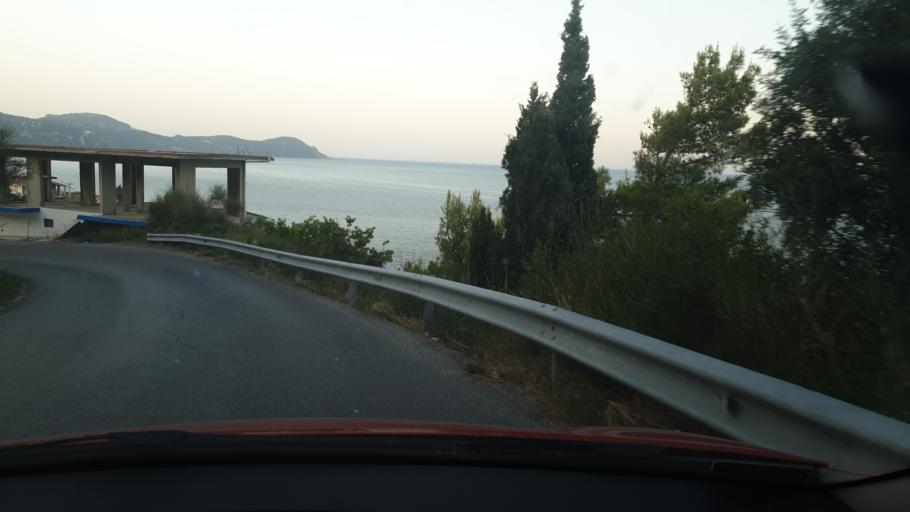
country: GR
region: Central Greece
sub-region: Nomos Evvoias
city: Oxilithos
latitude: 38.6009
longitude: 24.1202
